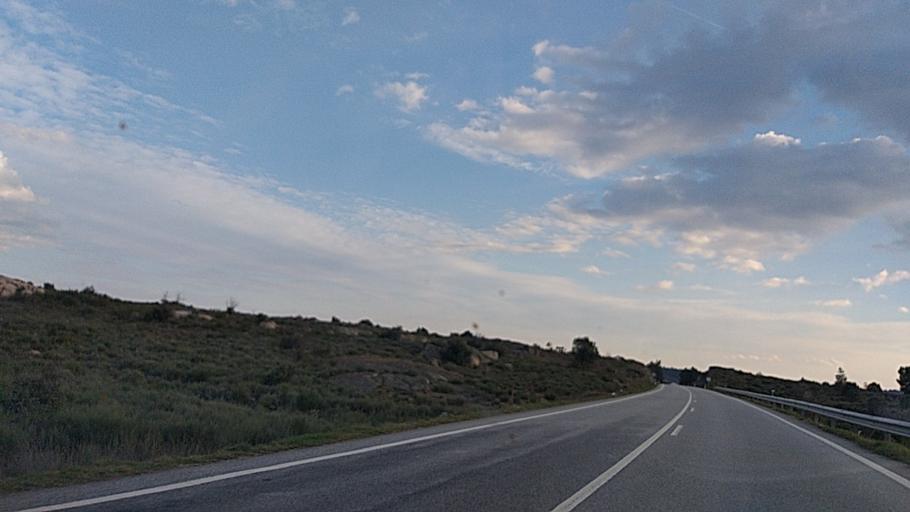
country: PT
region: Guarda
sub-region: Pinhel
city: Pinhel
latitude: 40.6823
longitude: -6.9505
